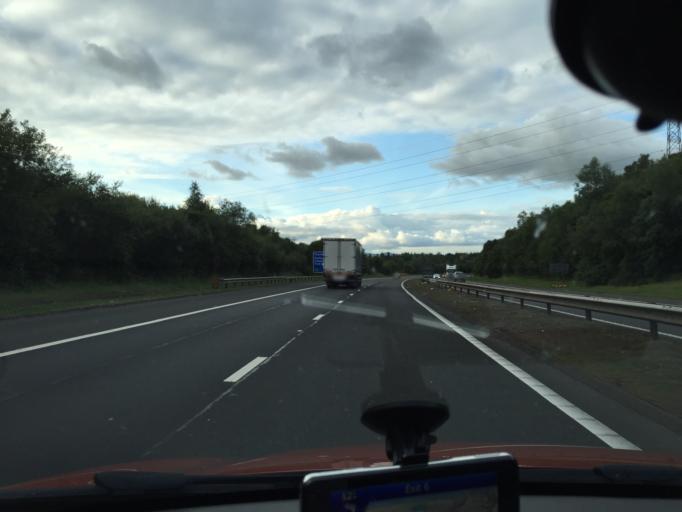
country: GB
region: Scotland
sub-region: North Lanarkshire
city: Chryston
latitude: 55.8787
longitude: -4.0808
